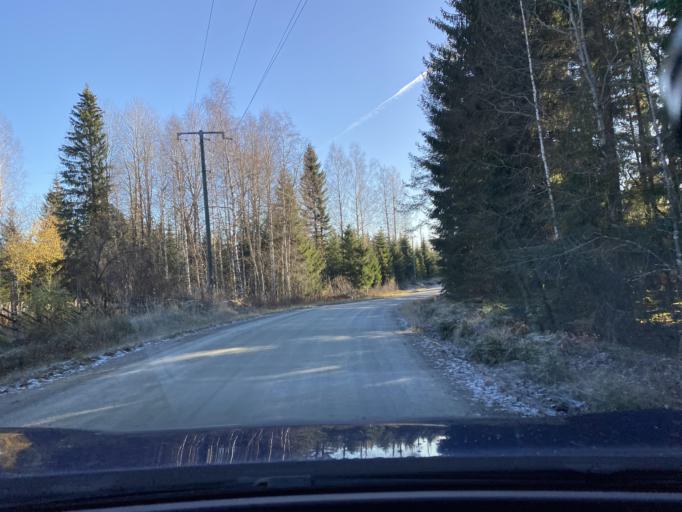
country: FI
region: Pirkanmaa
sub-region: Etelae-Pirkanmaa
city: Toijala
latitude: 61.0219
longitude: 23.8456
